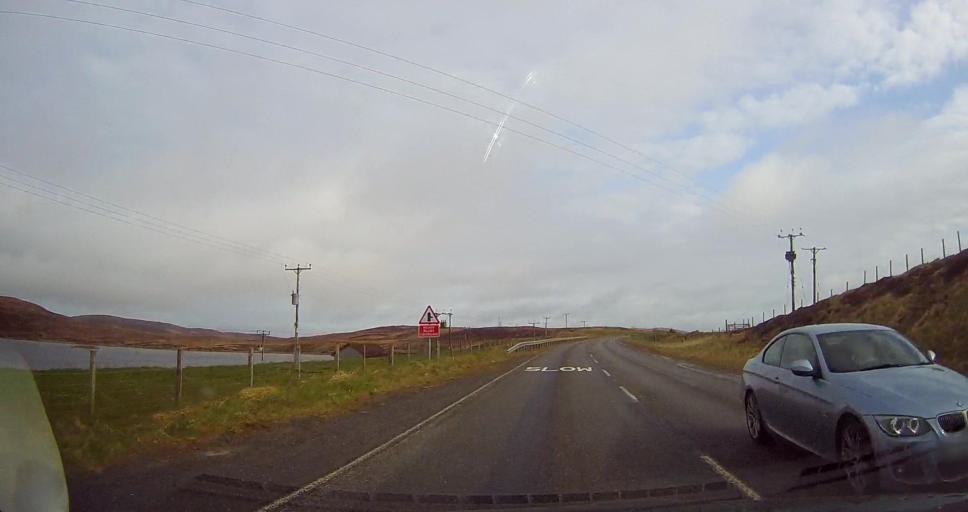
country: GB
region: Scotland
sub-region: Shetland Islands
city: Lerwick
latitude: 60.1124
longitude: -1.2189
